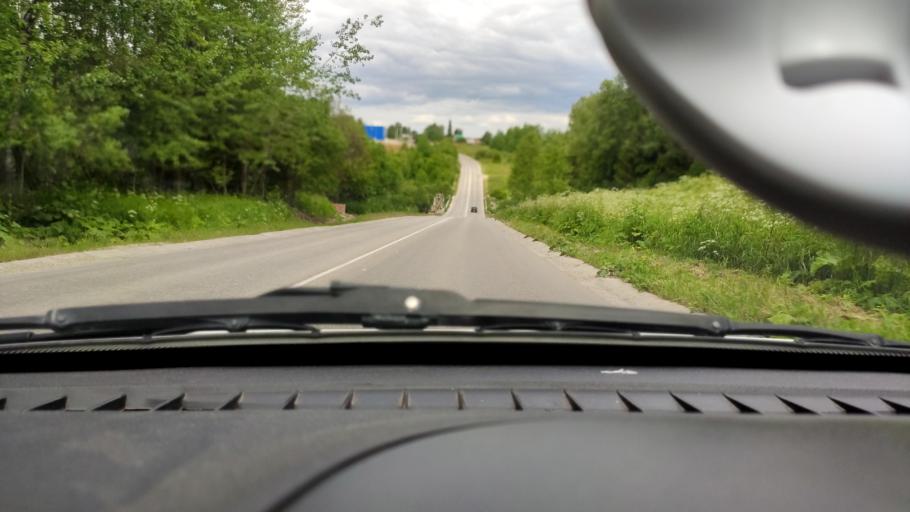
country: RU
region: Perm
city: Novyye Lyady
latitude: 58.0374
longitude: 56.6003
